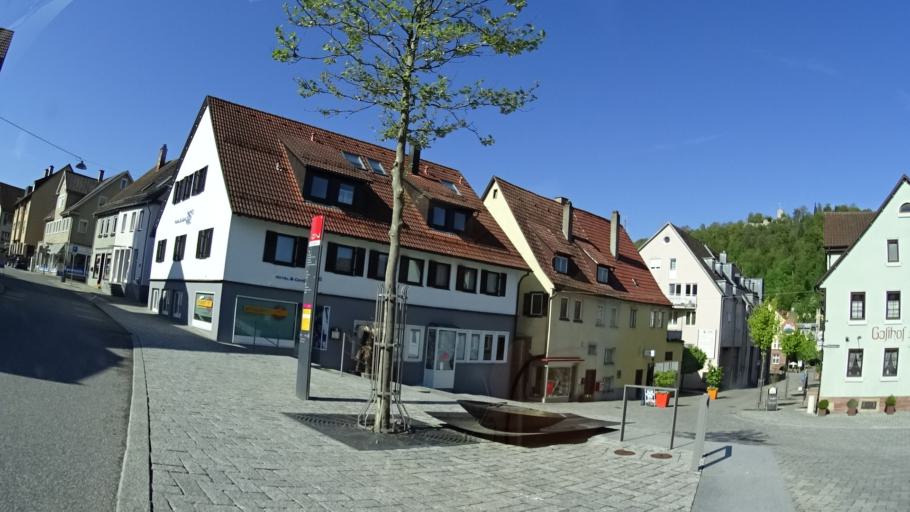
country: DE
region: Baden-Wuerttemberg
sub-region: Karlsruhe Region
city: Nagold
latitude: 48.5527
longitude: 8.7252
